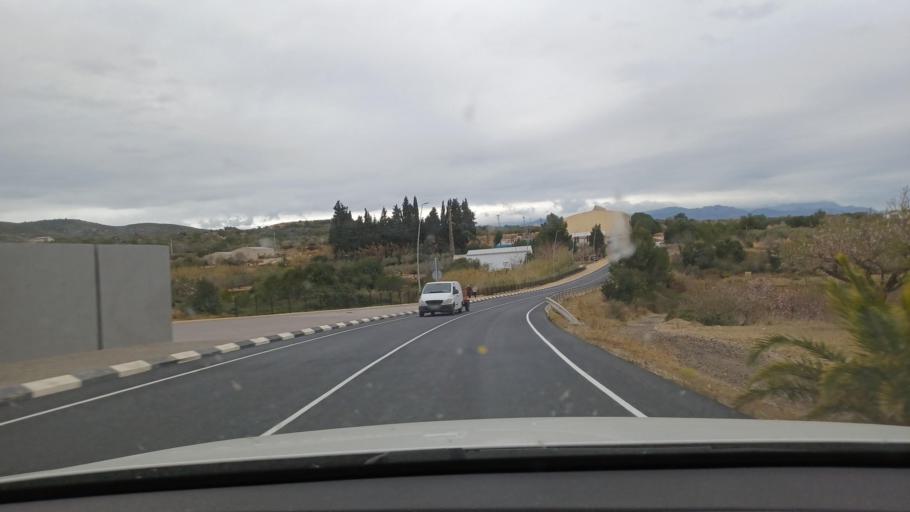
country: ES
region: Valencia
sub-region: Provincia de Castello
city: Traiguera
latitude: 40.5255
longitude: 0.2944
